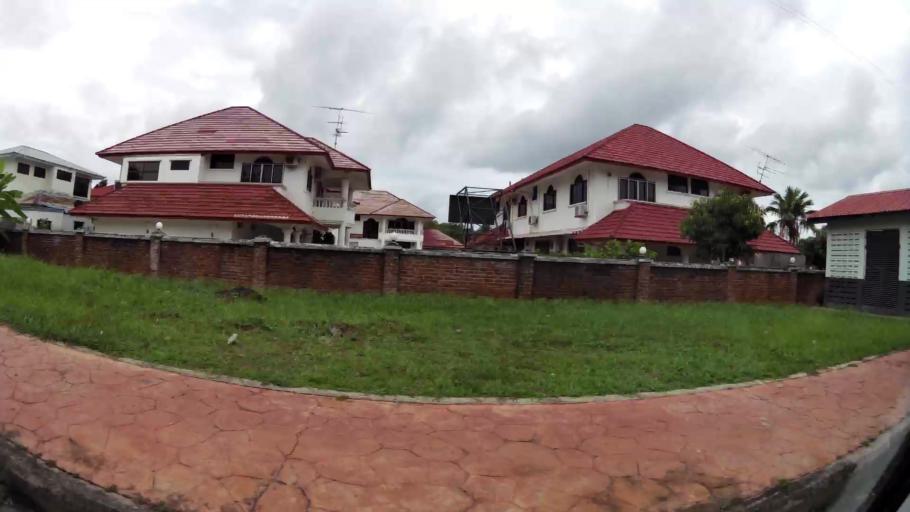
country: BN
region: Brunei and Muara
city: Bandar Seri Begawan
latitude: 4.8966
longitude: 114.9164
